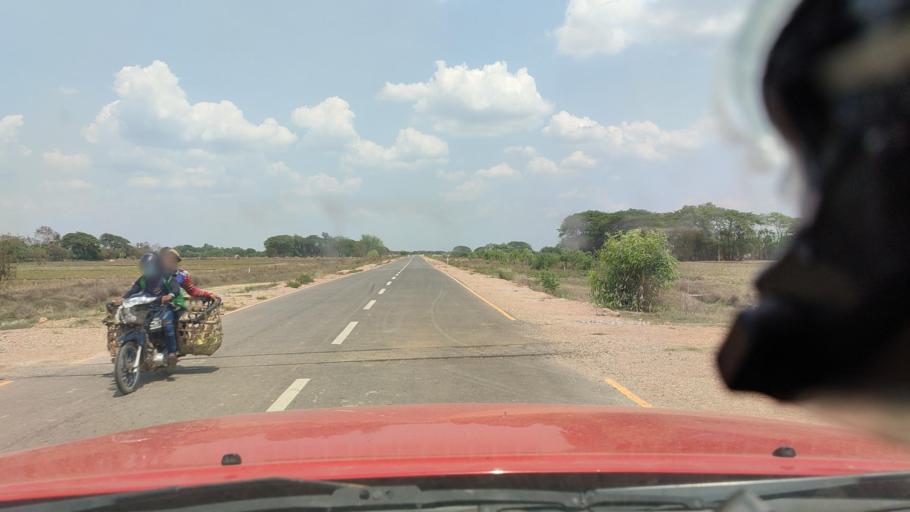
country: MM
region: Bago
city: Thanatpin
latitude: 17.0456
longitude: 96.3696
